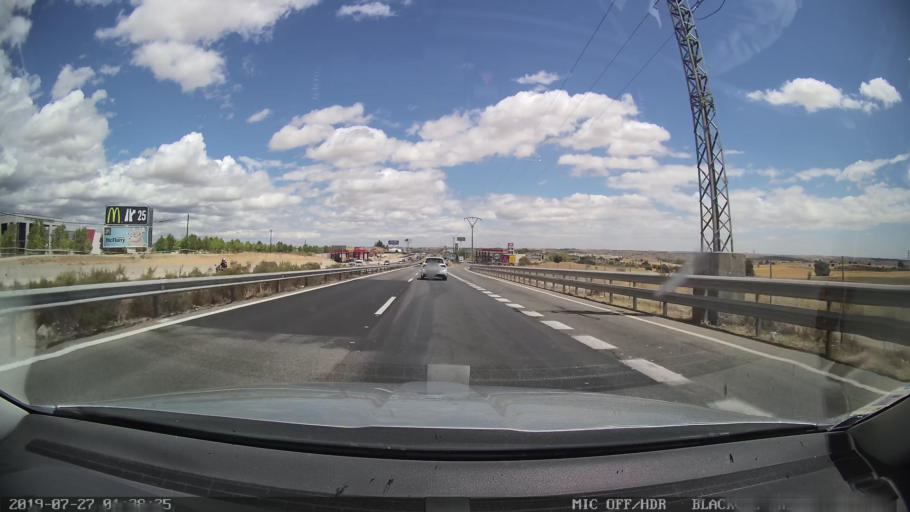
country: ES
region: Madrid
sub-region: Provincia de Madrid
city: Navalcarnero
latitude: 40.2917
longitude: -3.9828
